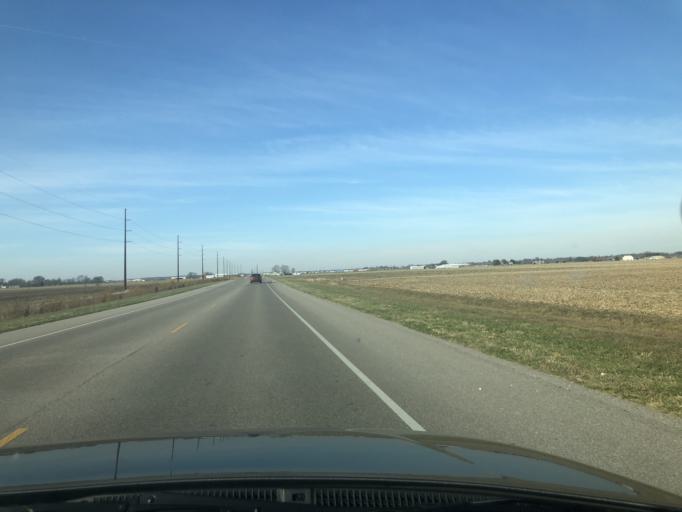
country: US
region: Indiana
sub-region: Warrick County
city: Newburgh
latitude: 37.9915
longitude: -87.4268
